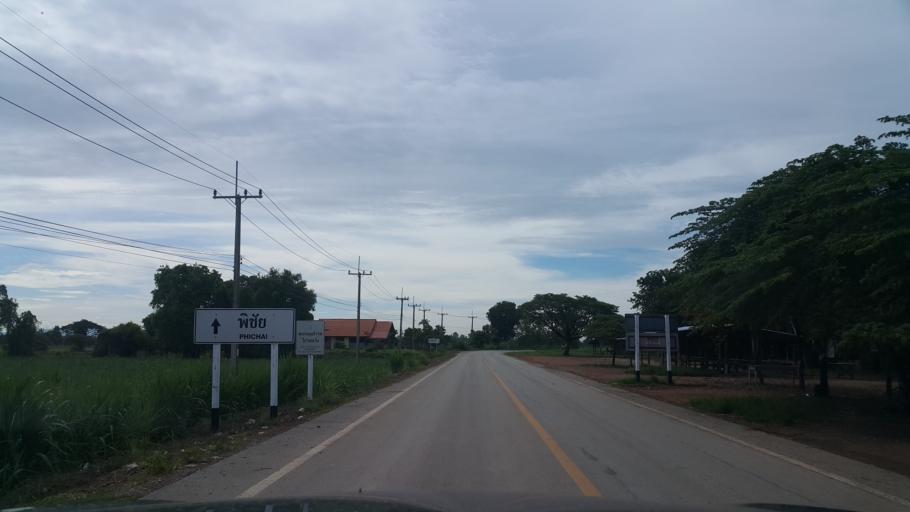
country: TH
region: Sukhothai
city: Si Nakhon
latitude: 17.2791
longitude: 99.9738
